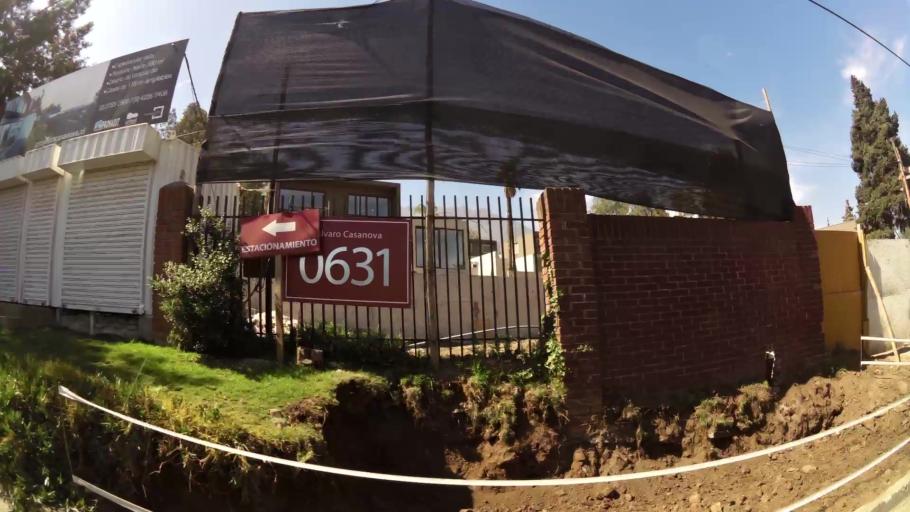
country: CL
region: Santiago Metropolitan
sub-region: Provincia de Santiago
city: Villa Presidente Frei, Nunoa, Santiago, Chile
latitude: -33.4581
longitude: -70.5224
